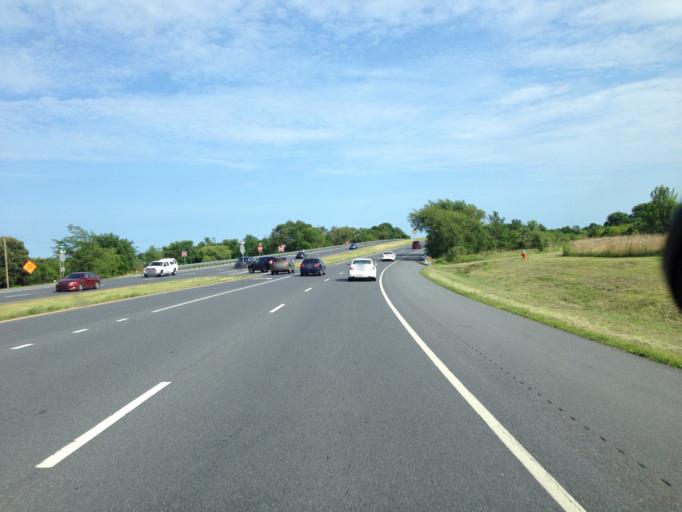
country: US
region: Delaware
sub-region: Sussex County
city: Lewes
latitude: 38.7542
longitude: -75.1922
